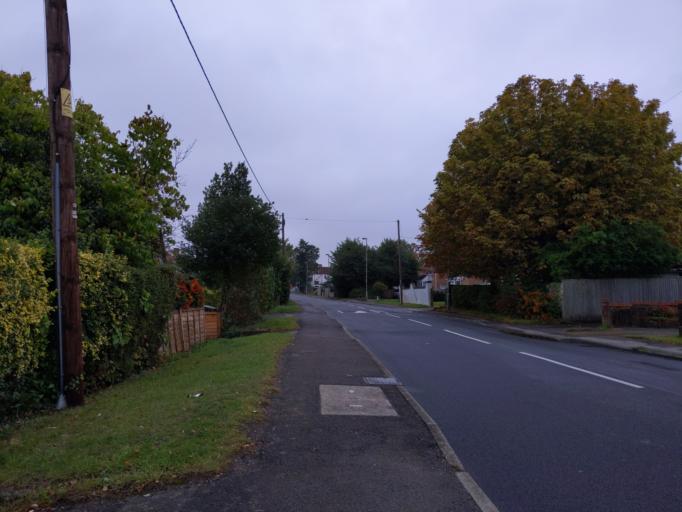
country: GB
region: England
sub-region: Oxfordshire
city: Oxford
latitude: 51.7237
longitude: -1.2488
